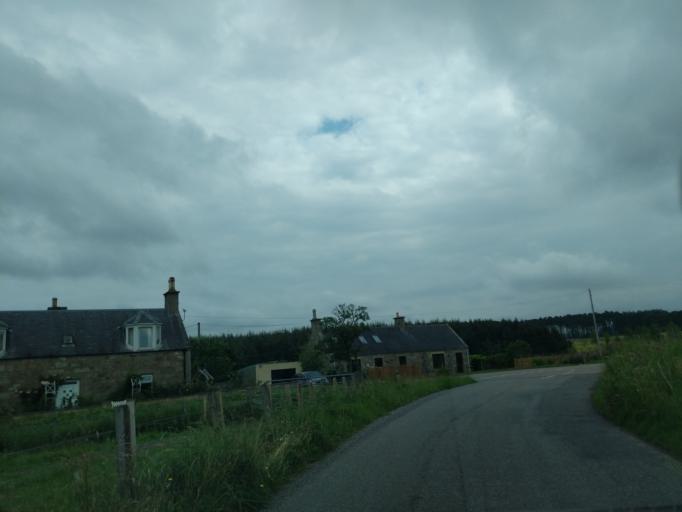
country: GB
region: Scotland
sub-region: Moray
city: Rothes
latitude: 57.4914
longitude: -3.2177
